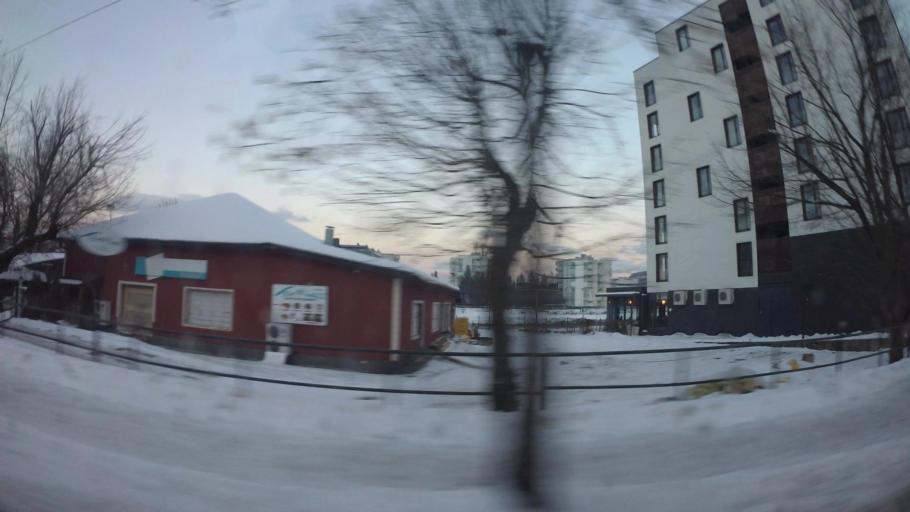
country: BA
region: Federation of Bosnia and Herzegovina
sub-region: Kanton Sarajevo
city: Sarajevo
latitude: 43.8291
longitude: 18.3045
